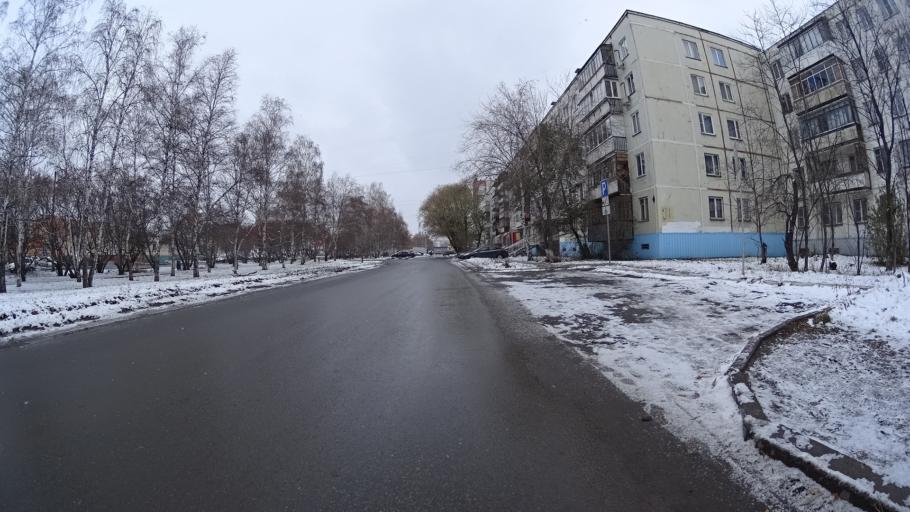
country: RU
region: Chelyabinsk
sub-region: Gorod Chelyabinsk
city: Chelyabinsk
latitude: 55.1926
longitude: 61.3220
